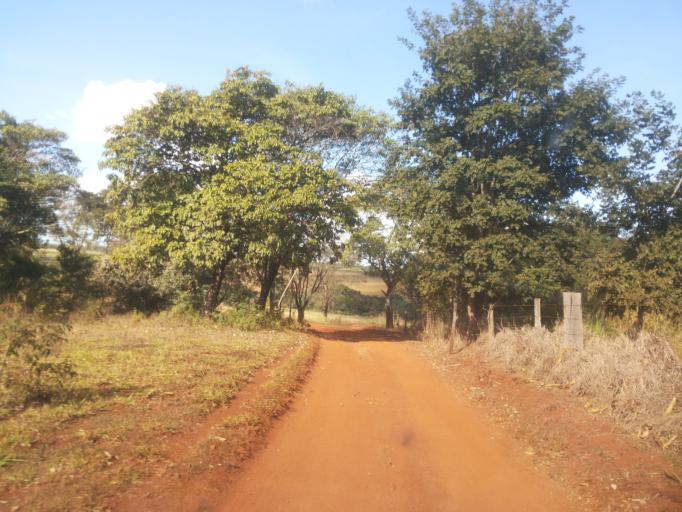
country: BR
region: Minas Gerais
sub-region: Capinopolis
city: Capinopolis
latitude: -18.6020
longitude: -49.4917
